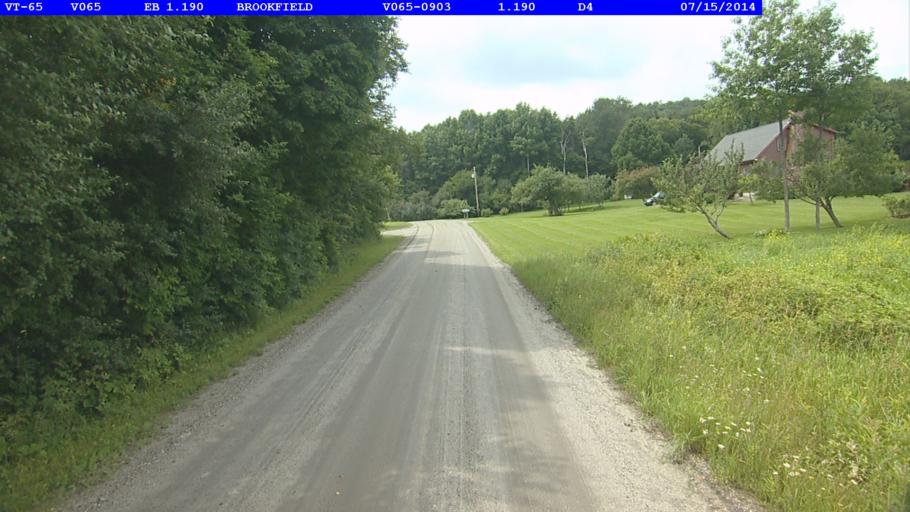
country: US
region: Vermont
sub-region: Washington County
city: Northfield
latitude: 44.0536
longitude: -72.6268
